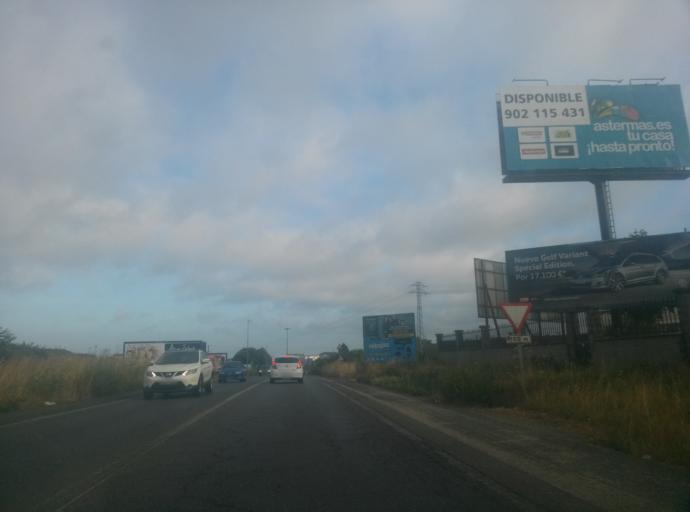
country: ES
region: Galicia
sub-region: Provincia de Lugo
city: Lugo
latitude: 43.0337
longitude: -7.5642
